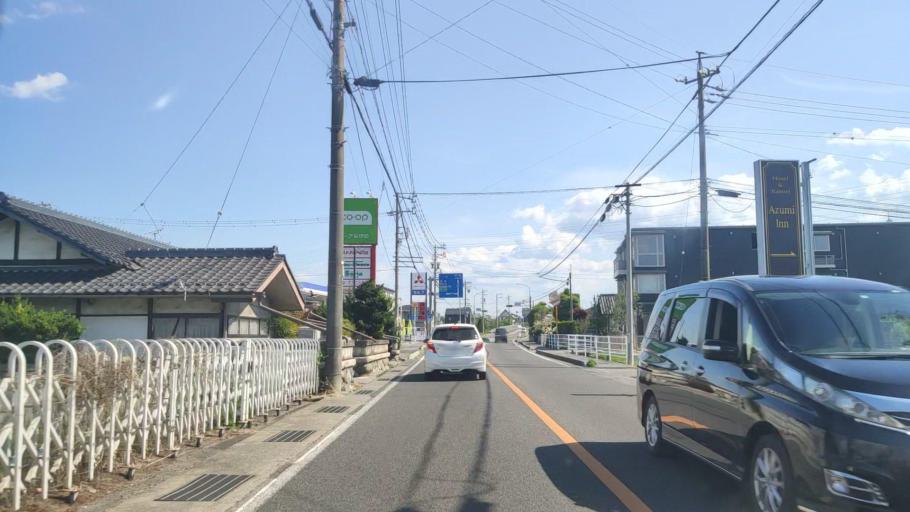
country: JP
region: Nagano
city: Toyoshina
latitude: 36.2869
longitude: 137.9079
